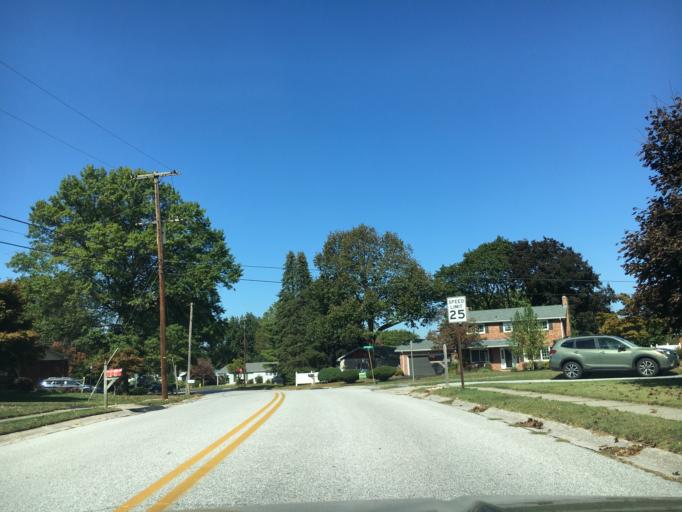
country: US
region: Pennsylvania
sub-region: York County
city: East York
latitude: 39.9652
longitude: -76.6740
